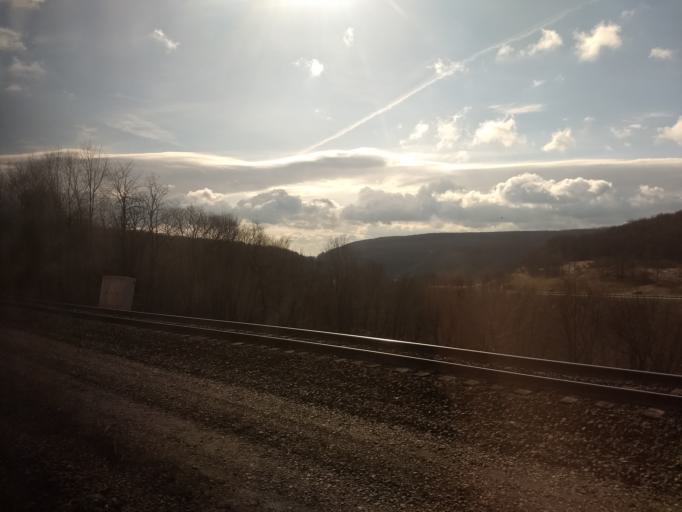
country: US
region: Pennsylvania
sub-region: Cambria County
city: Gallitzin
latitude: 40.4805
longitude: -78.5225
